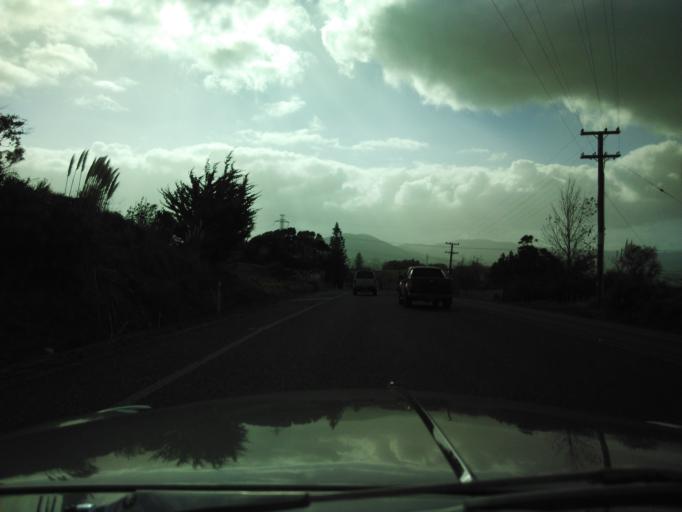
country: NZ
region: Auckland
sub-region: Auckland
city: Wellsford
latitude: -36.1837
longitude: 174.4502
